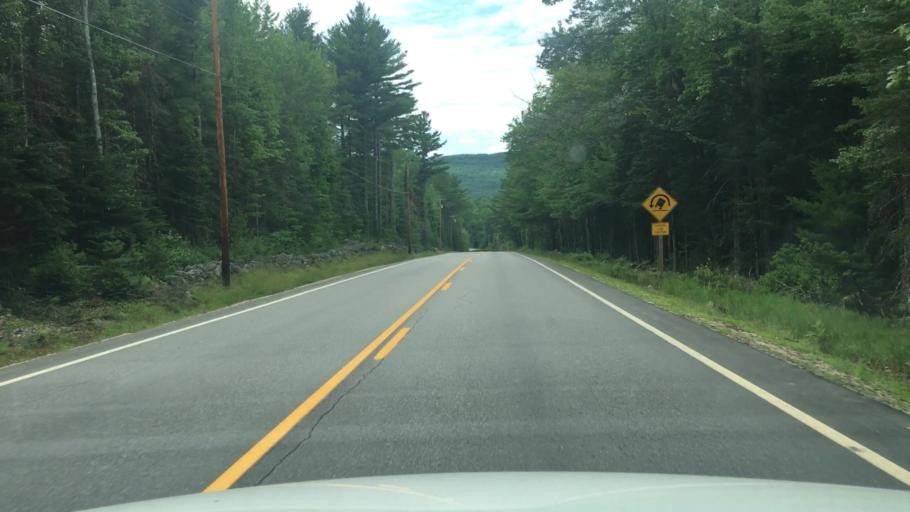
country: US
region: Maine
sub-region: Oxford County
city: West Paris
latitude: 44.3666
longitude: -70.4915
